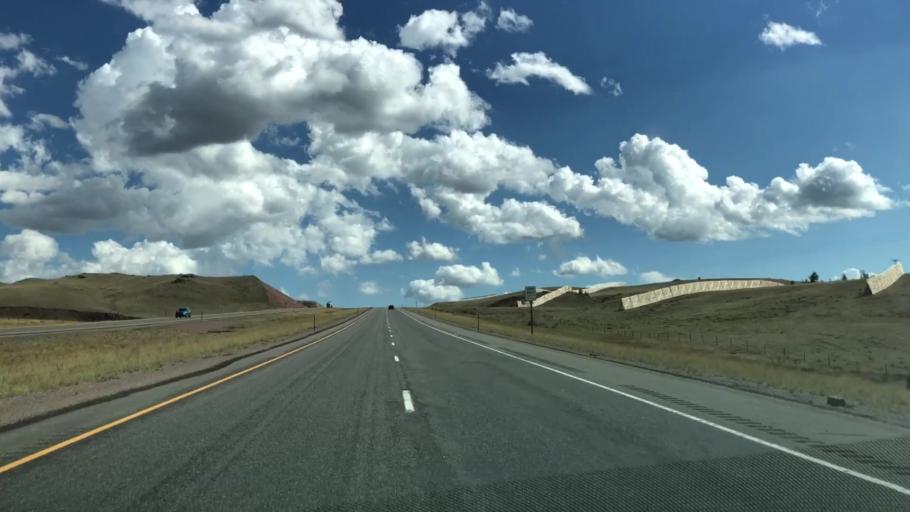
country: US
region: Wyoming
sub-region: Albany County
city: Laramie
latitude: 41.0606
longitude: -105.4748
